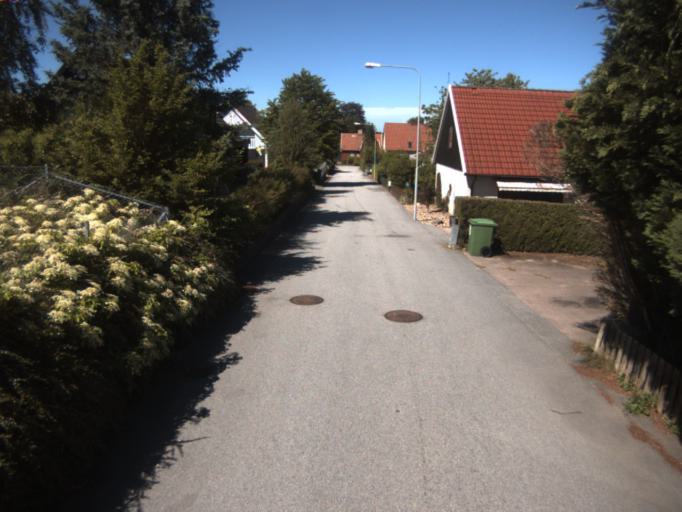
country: SE
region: Skane
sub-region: Helsingborg
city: Morarp
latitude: 56.0543
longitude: 12.8708
